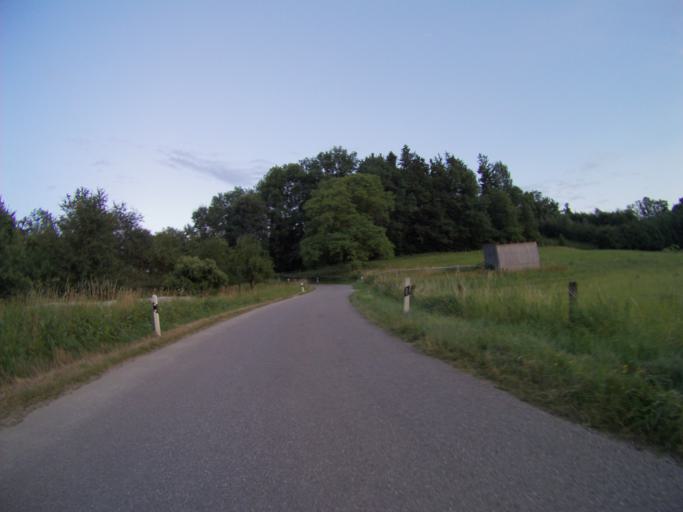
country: DE
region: Bavaria
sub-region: Upper Bavaria
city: Marzling
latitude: 48.4374
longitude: 11.7971
